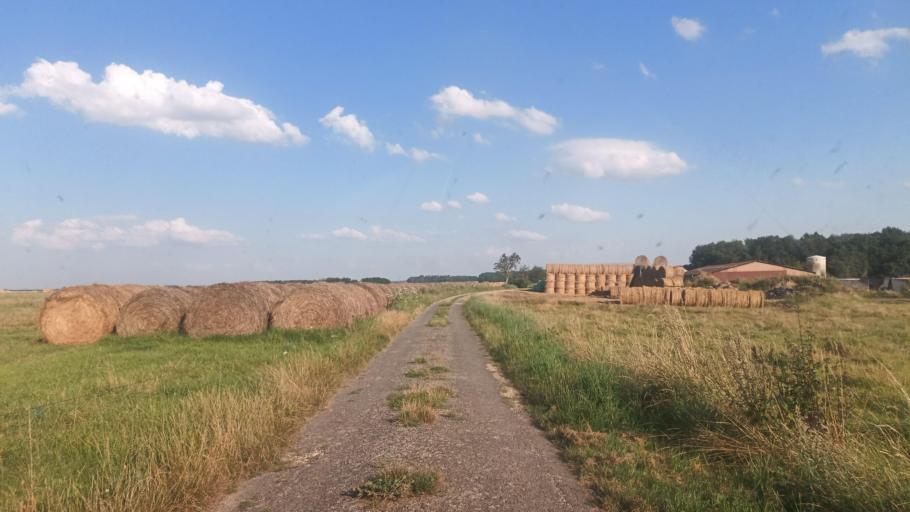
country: FR
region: Bourgogne
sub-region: Departement de l'Yonne
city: Saint-Valerien
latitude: 48.2239
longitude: 3.0828
